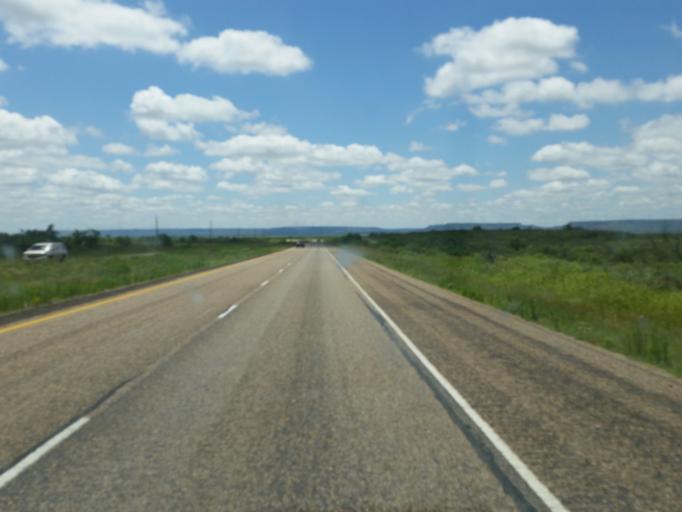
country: US
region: Texas
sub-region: Garza County
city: Post
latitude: 33.0828
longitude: -101.2412
